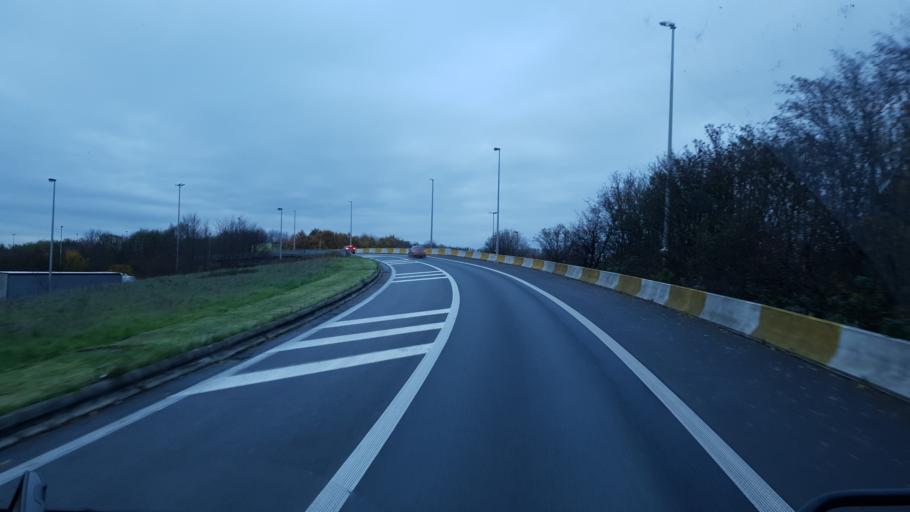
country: BE
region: Flanders
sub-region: Provincie Oost-Vlaanderen
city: Destelbergen
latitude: 51.0490
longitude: 3.8228
